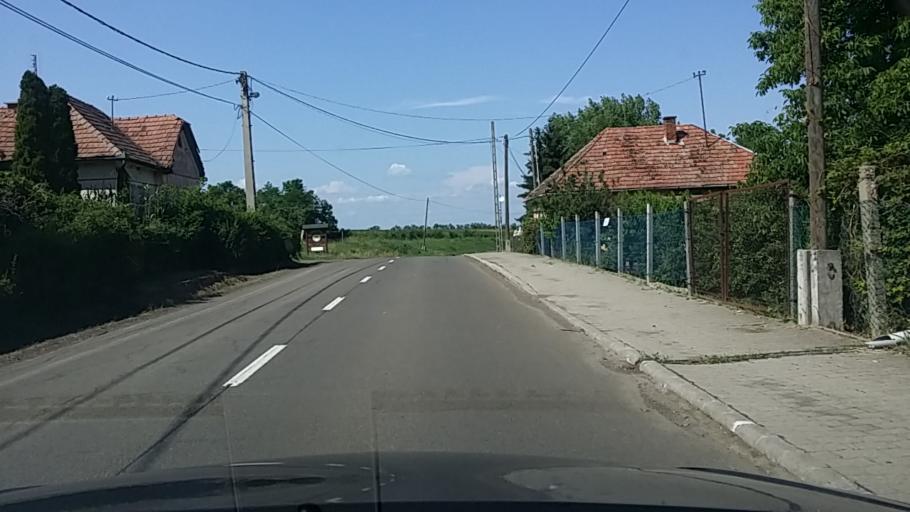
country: SK
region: Nitriansky
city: Sahy
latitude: 48.0258
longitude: 18.8974
